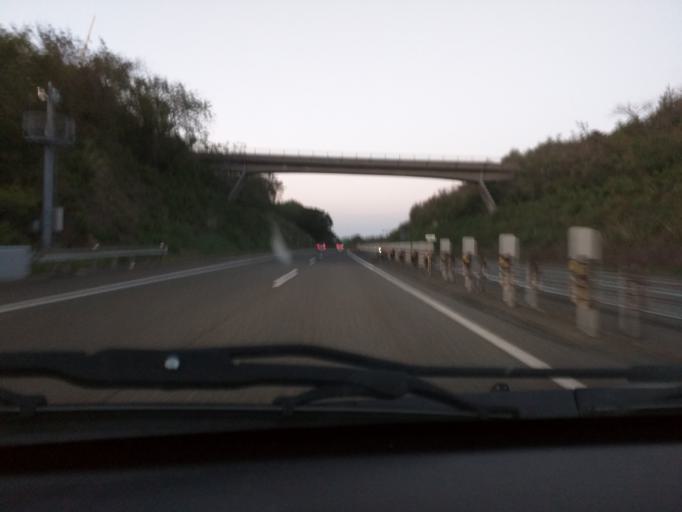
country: JP
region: Niigata
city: Kashiwazaki
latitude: 37.3435
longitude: 138.4896
